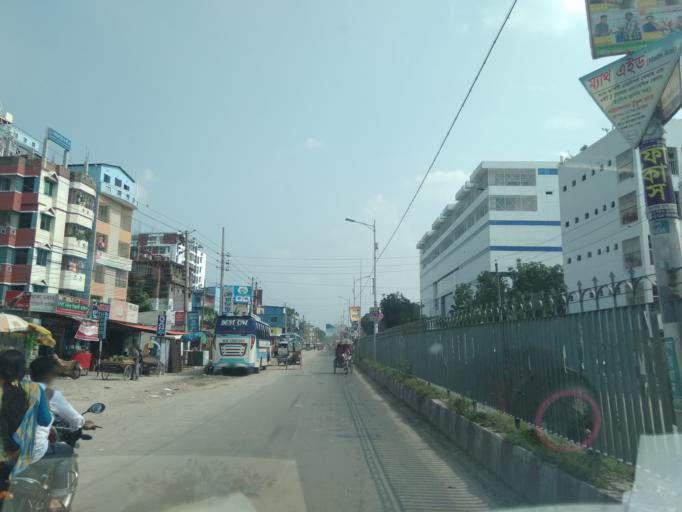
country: BD
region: Rangpur Division
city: Rangpur
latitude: 25.7636
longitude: 89.2315
